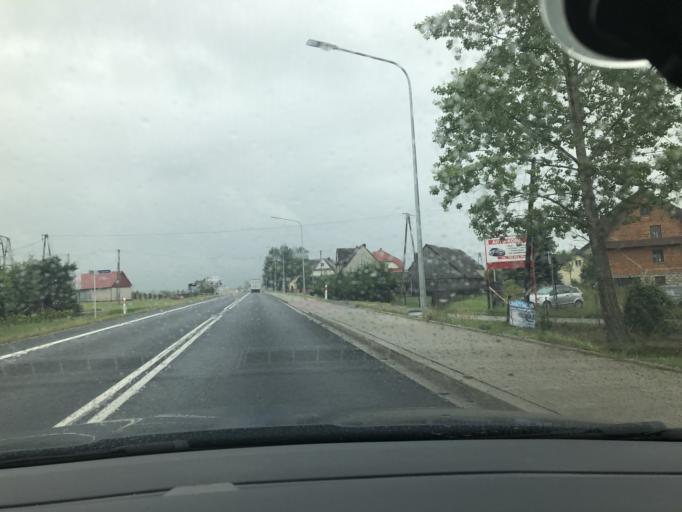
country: PL
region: Lesser Poland Voivodeship
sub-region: Powiat nowotarski
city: Jablonka
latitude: 49.4577
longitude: 19.6898
